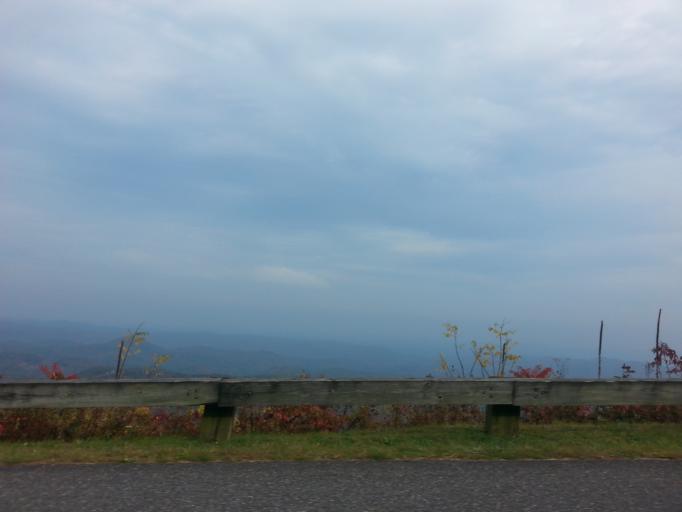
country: US
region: North Carolina
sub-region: Ashe County
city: Jefferson
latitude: 36.2957
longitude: -81.3667
